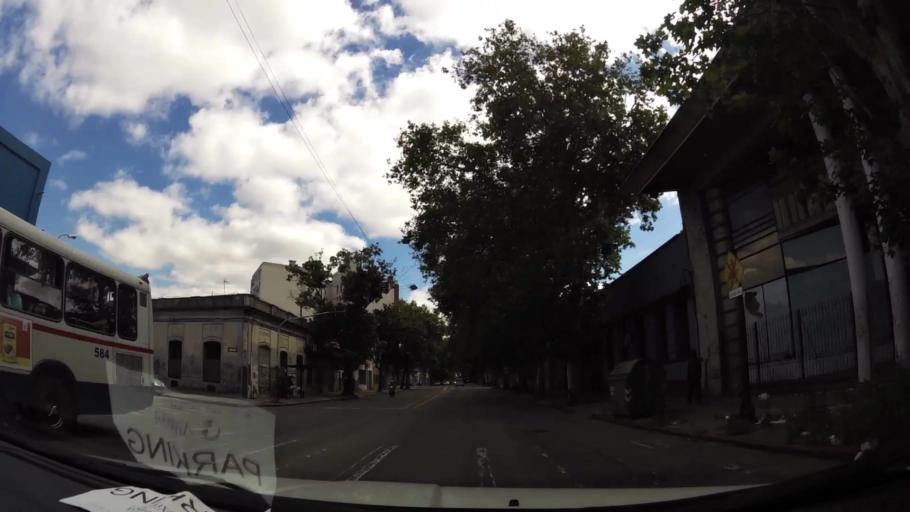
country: UY
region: Montevideo
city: Montevideo
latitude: -34.8842
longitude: -56.1868
